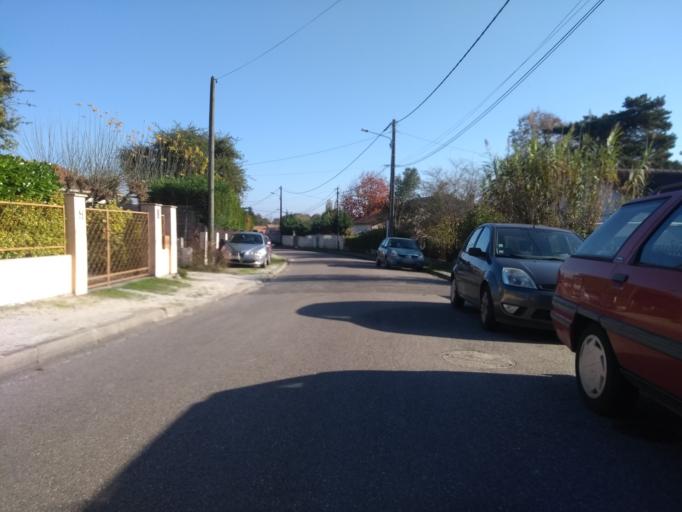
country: FR
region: Aquitaine
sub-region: Departement de la Gironde
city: Leognan
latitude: 44.7405
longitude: -0.6017
